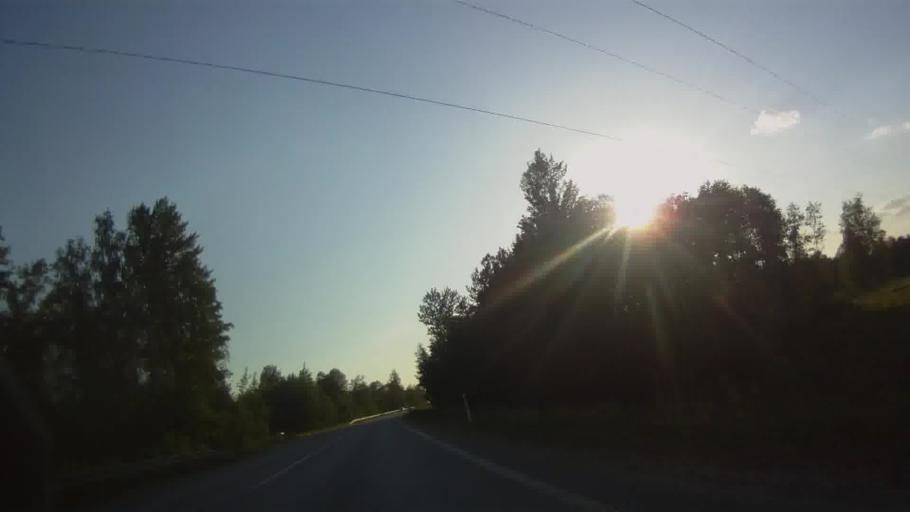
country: LV
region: Livani
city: Livani
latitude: 56.5292
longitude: 26.3725
